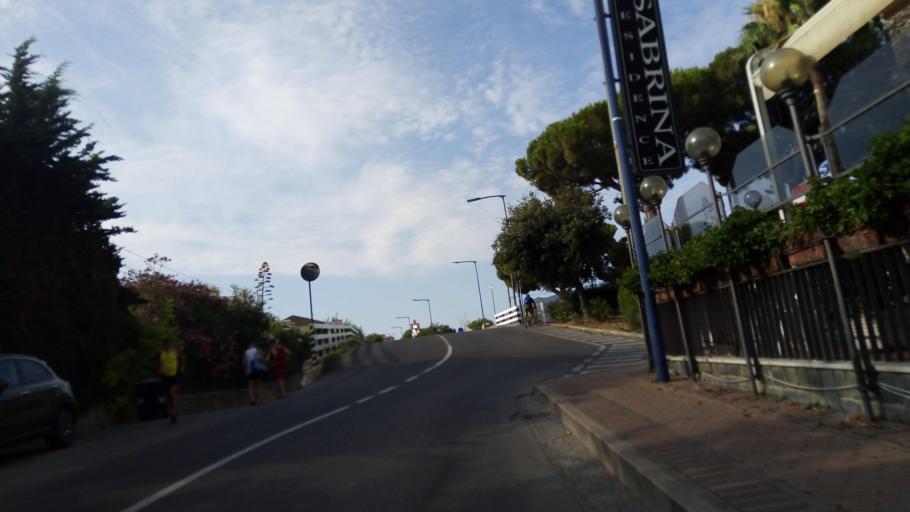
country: IT
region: Liguria
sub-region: Provincia di Savona
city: Ceriale
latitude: 44.0846
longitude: 8.2275
